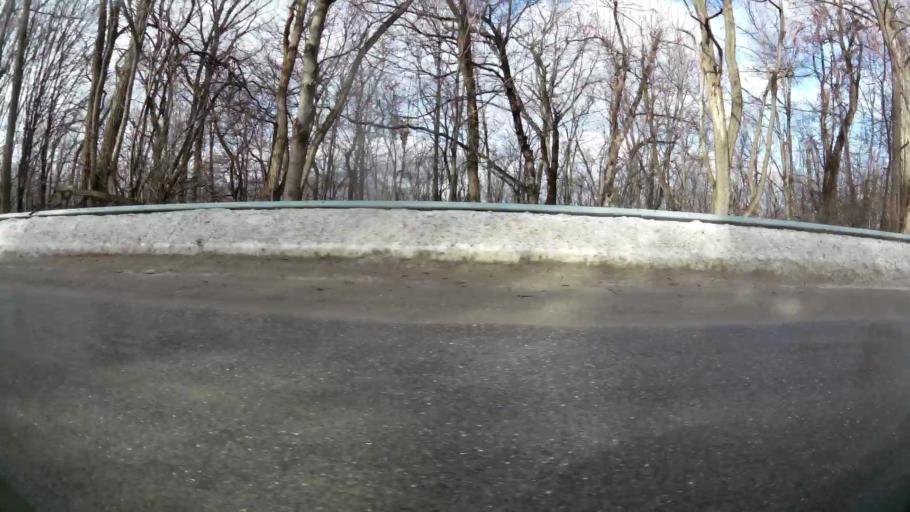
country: BG
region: Sofiya
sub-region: Obshtina Bozhurishte
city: Bozhurishte
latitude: 42.6364
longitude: 23.2248
